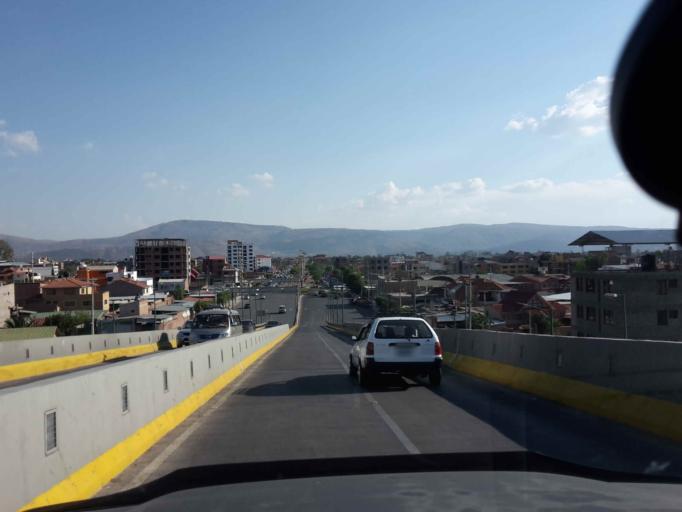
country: BO
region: Cochabamba
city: Cochabamba
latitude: -17.3938
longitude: -66.1844
